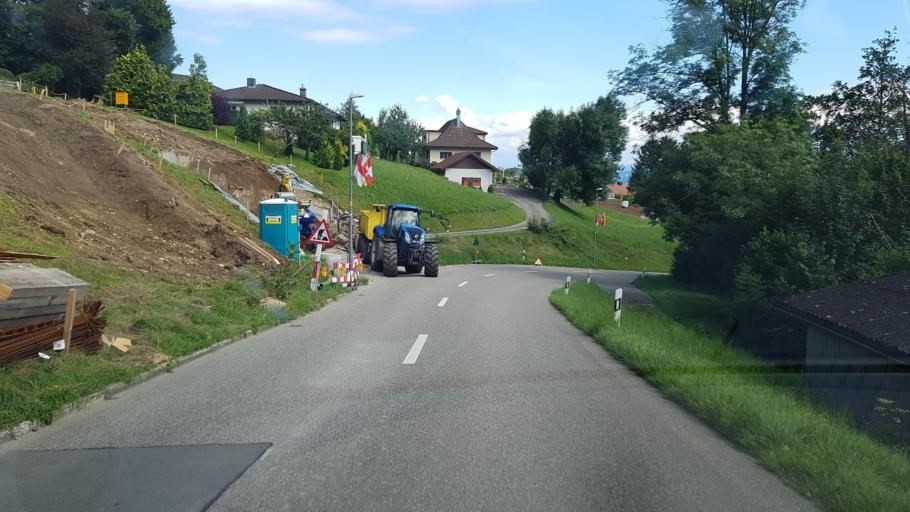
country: CH
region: Solothurn
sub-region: Bezirk Lebern
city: Riedholz
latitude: 47.2558
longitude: 7.5782
